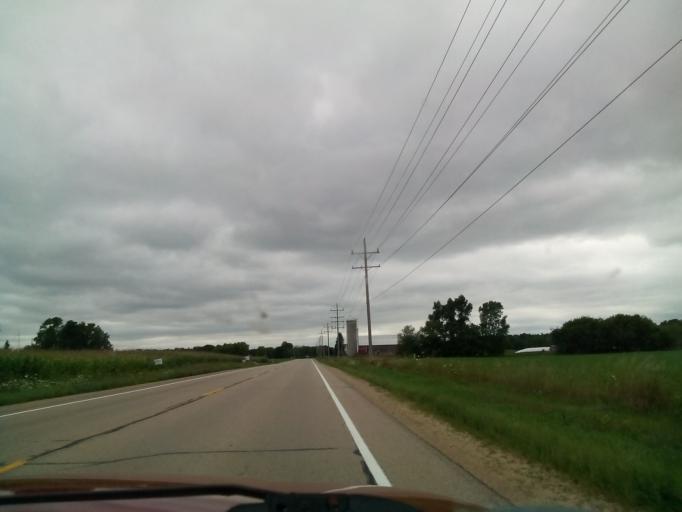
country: US
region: Wisconsin
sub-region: Waupaca County
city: New London
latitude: 44.2658
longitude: -88.8024
